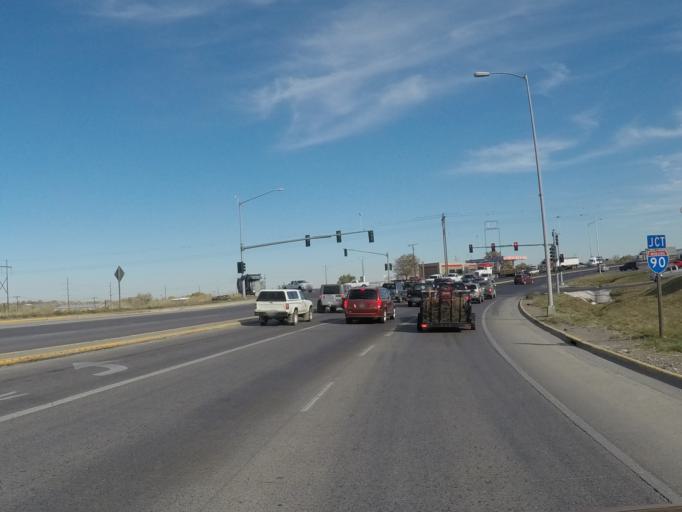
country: US
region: Montana
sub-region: Yellowstone County
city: Billings
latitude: 45.7970
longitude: -108.4615
